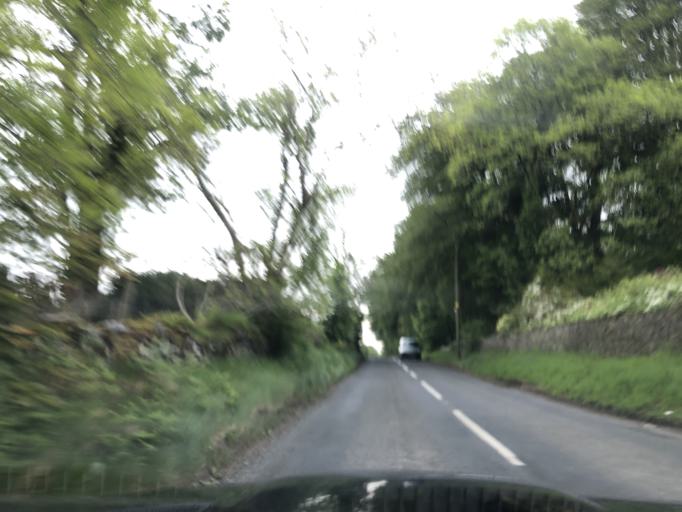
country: GB
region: Northern Ireland
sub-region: Down District
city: Castlewellan
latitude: 54.2233
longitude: -5.9667
